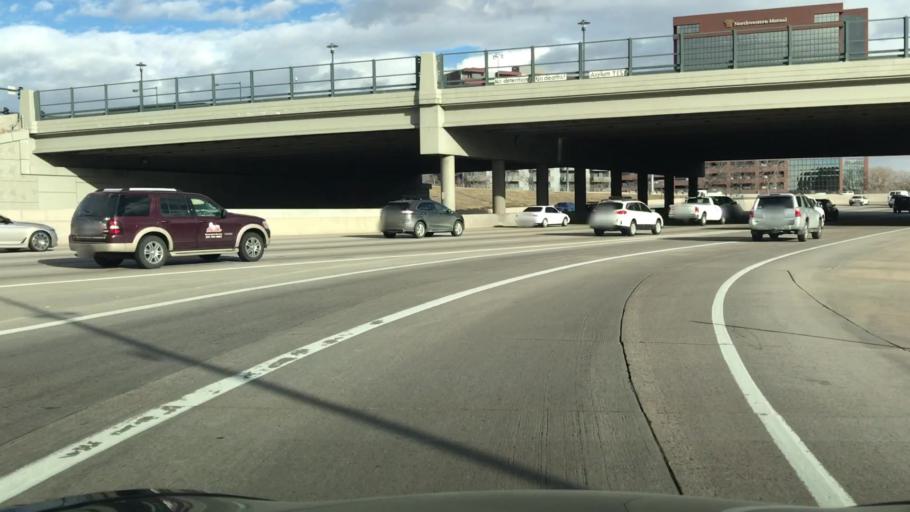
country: US
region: Colorado
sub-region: Arapahoe County
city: Glendale
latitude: 39.6827
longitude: -104.9413
